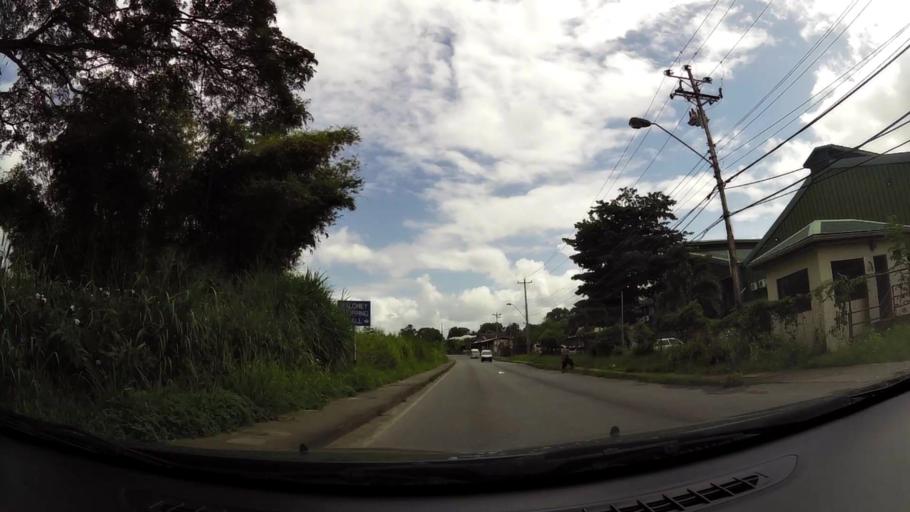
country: TT
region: Tunapuna/Piarco
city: Arouca
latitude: 10.6298
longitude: -61.3204
